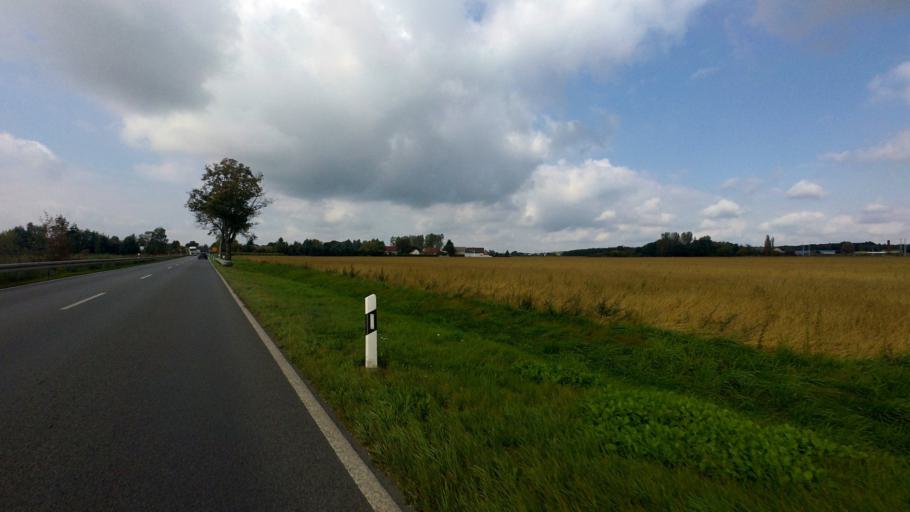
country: DE
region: Brandenburg
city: Hohenleipisch
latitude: 51.4699
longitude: 13.5720
